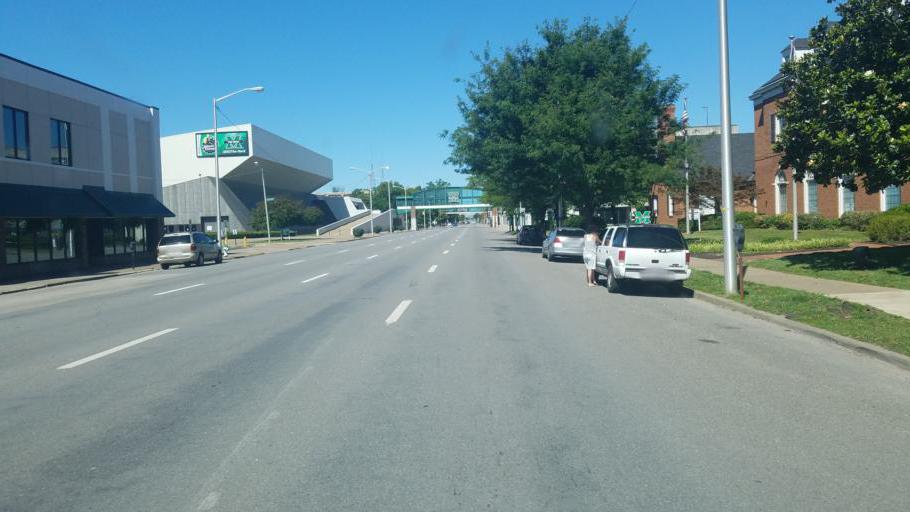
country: US
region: West Virginia
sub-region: Cabell County
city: Huntington
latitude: 38.4256
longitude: -82.4236
